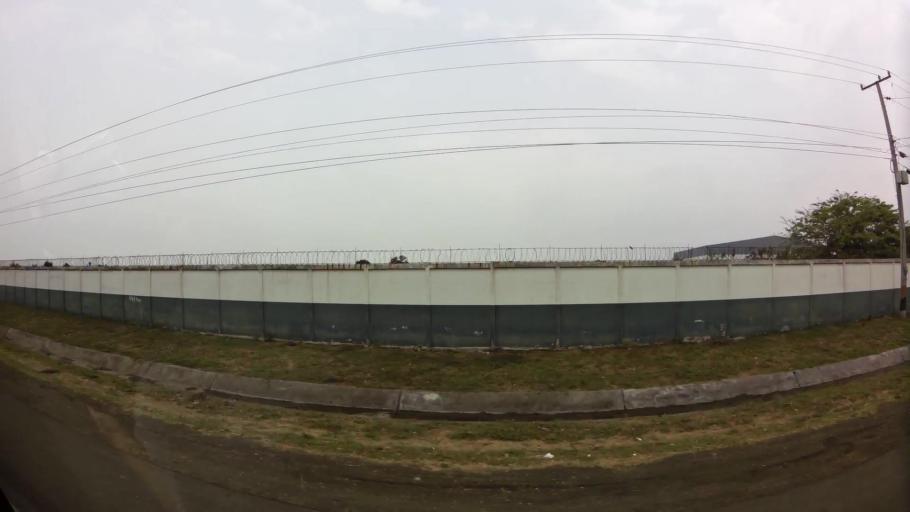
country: NI
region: Chinandega
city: Chinandega
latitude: 12.6179
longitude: -87.1087
